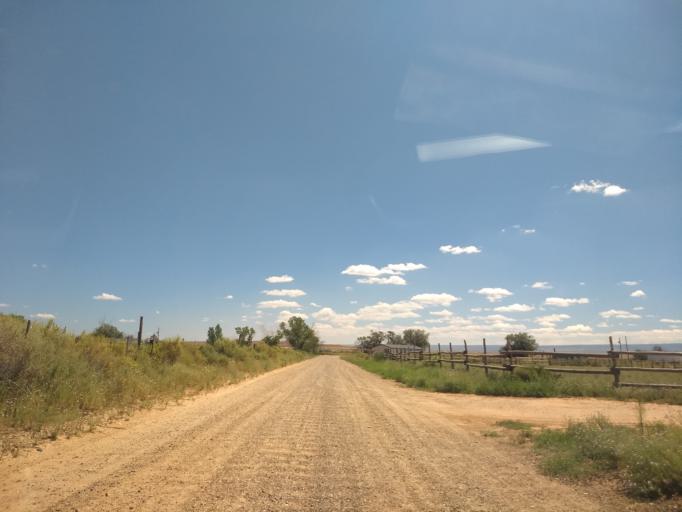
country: US
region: Arizona
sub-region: Coconino County
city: Fredonia
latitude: 36.9326
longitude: -112.5378
